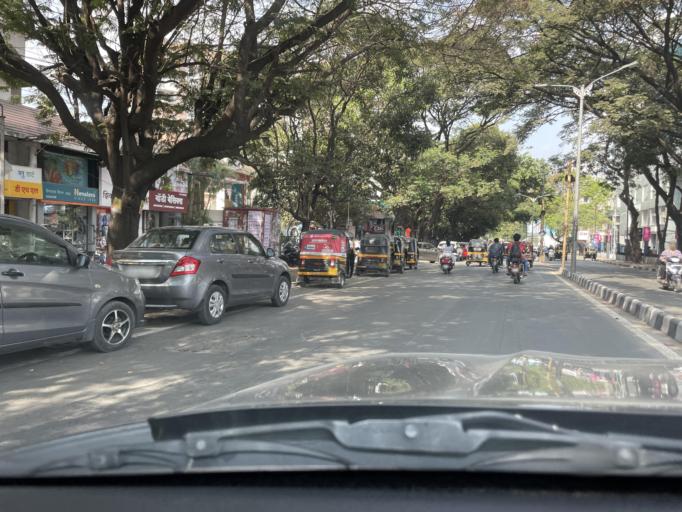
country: IN
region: Maharashtra
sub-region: Pune Division
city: Pune
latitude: 18.4907
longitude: 73.9000
